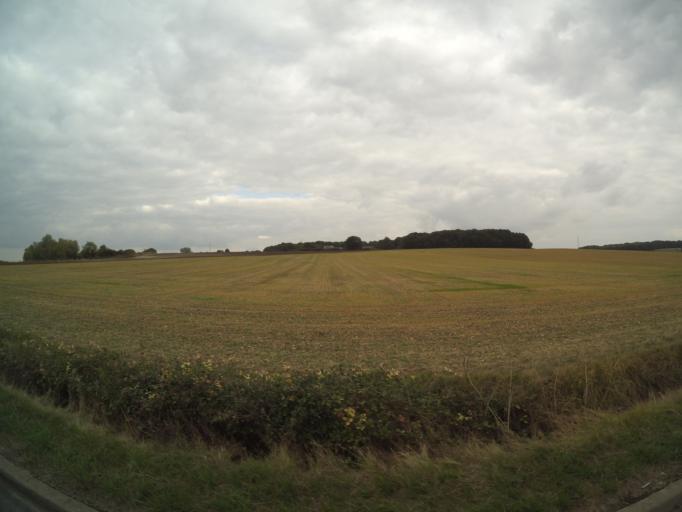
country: FR
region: Centre
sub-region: Departement d'Indre-et-Loire
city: Auzouer-en-Touraine
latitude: 47.5062
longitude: 0.9234
